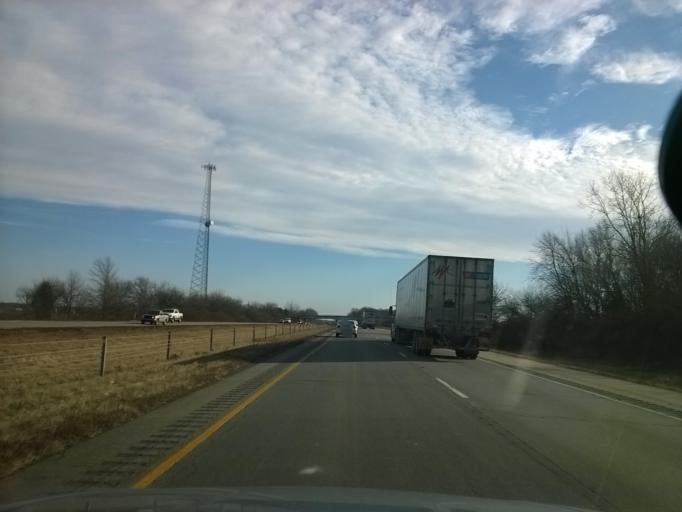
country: US
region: Indiana
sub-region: Johnson County
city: Franklin
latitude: 39.4582
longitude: -86.0008
